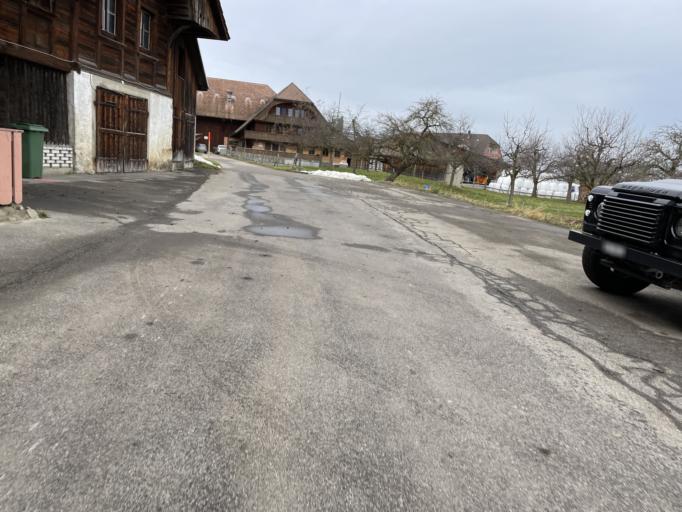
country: CH
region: Bern
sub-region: Bern-Mittelland District
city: Toffen
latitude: 46.8666
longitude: 7.5218
